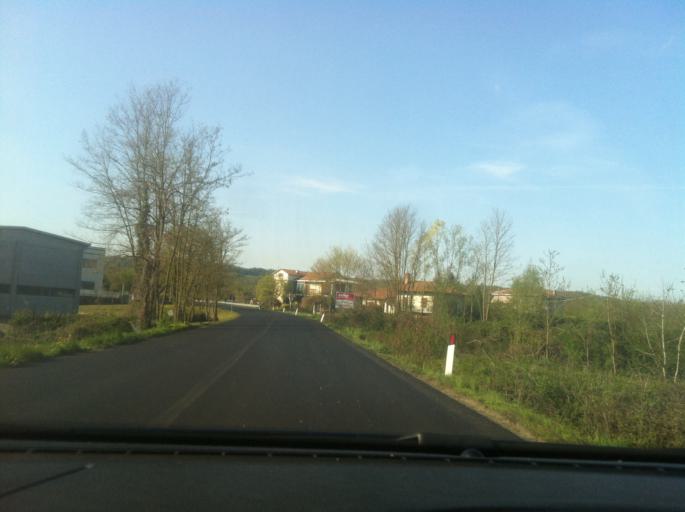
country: IT
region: Piedmont
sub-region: Provincia di Torino
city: Mercenasco
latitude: 45.3683
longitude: 7.8772
